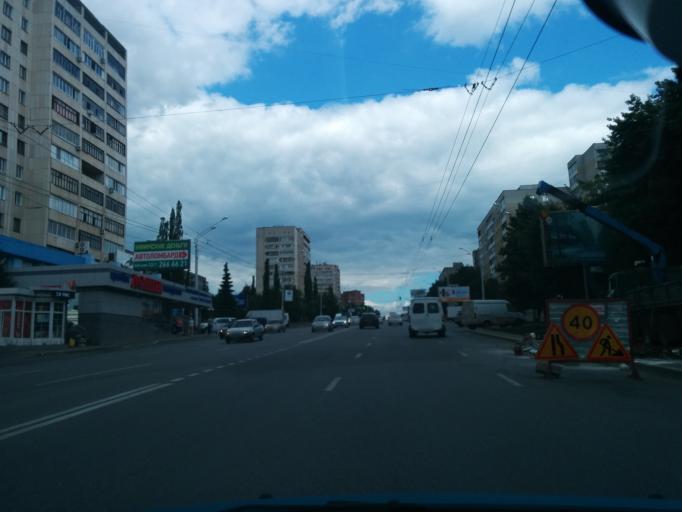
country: RU
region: Bashkortostan
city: Ufa
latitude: 54.7274
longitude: 55.9770
